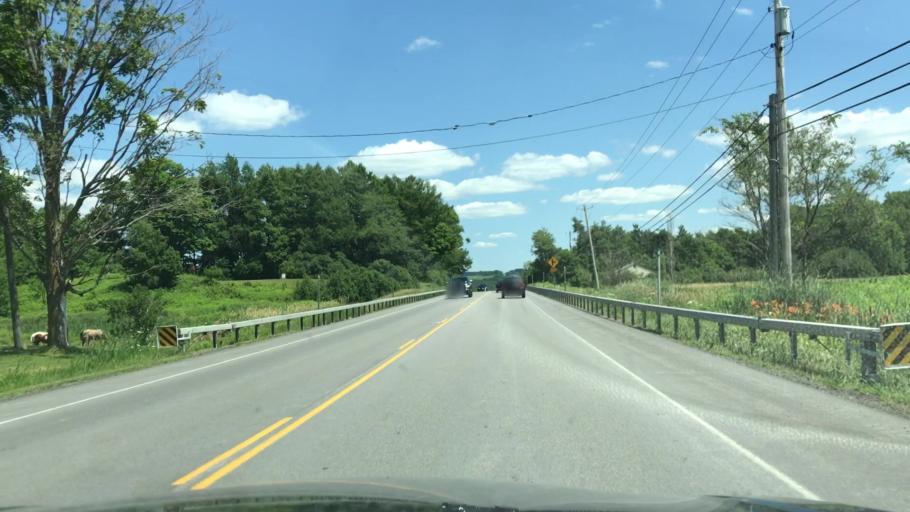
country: US
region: New York
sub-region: Wyoming County
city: Attica
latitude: 42.7702
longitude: -78.4022
